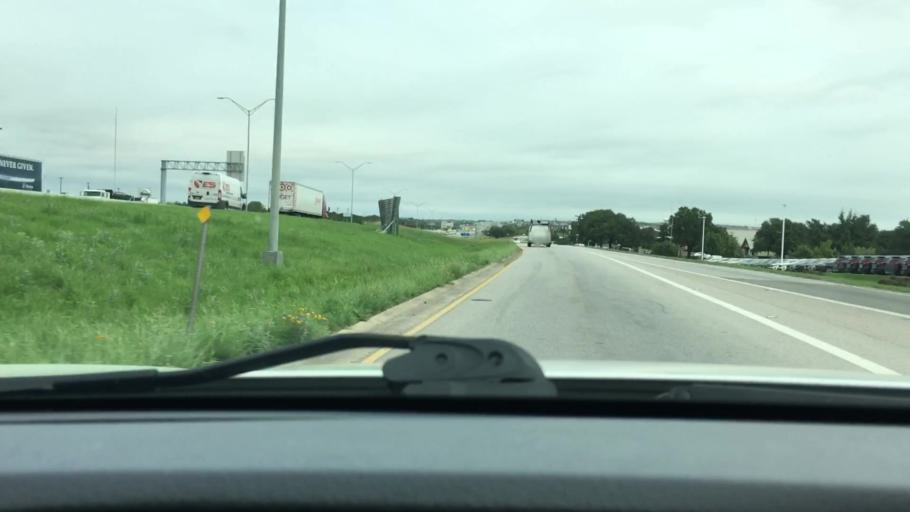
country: US
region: Texas
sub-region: Williamson County
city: Round Rock
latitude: 30.5407
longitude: -97.6919
